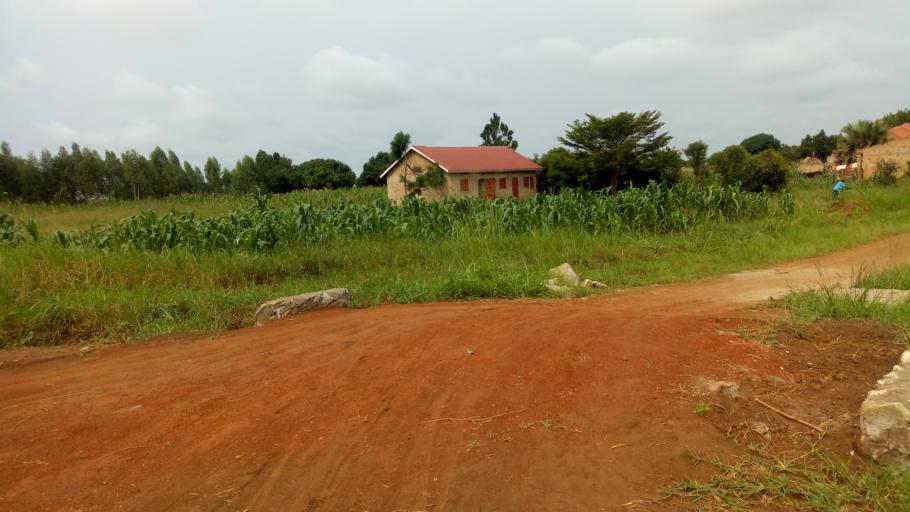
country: UG
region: Western Region
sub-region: Kiryandongo District
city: Kiryandongo
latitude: 1.8020
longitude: 32.0153
